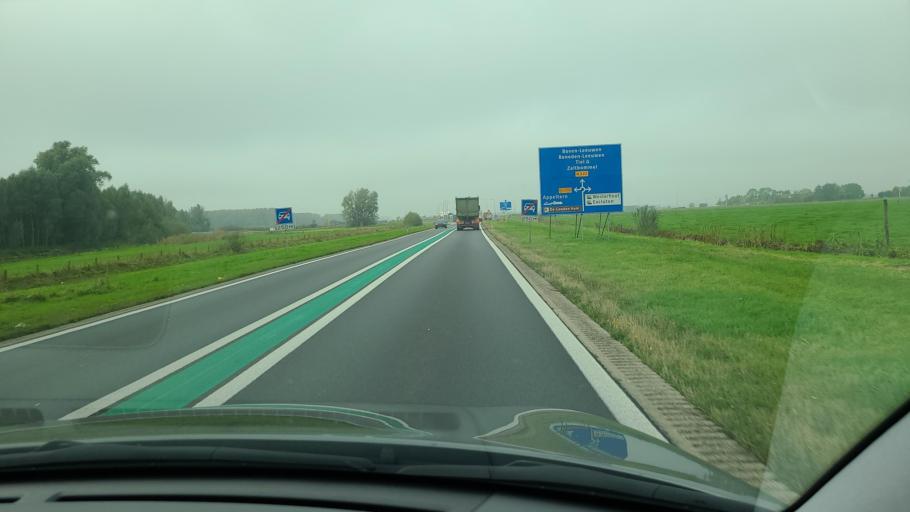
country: NL
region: Gelderland
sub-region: Gemeente Druten
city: Druten
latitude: 51.8678
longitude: 5.5898
